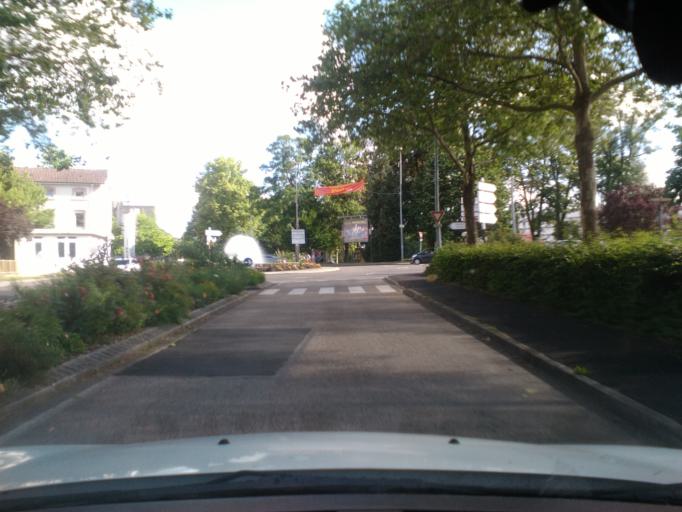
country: FR
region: Lorraine
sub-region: Departement des Vosges
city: Epinal
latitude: 48.1848
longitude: 6.4456
